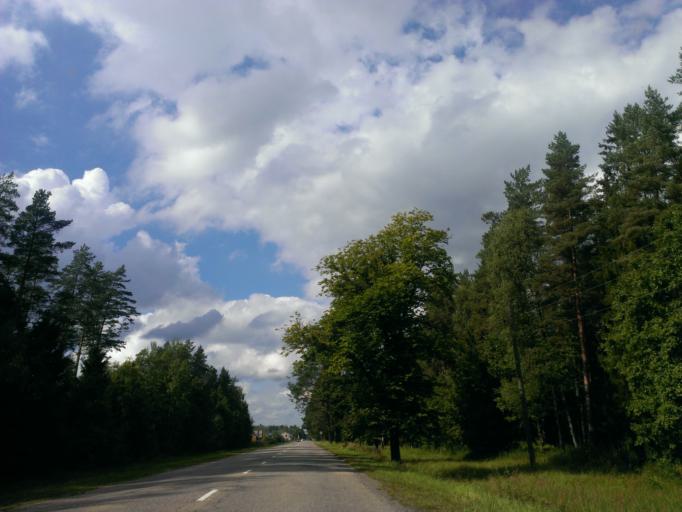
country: LV
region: Garkalne
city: Garkalne
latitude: 56.9668
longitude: 24.4884
